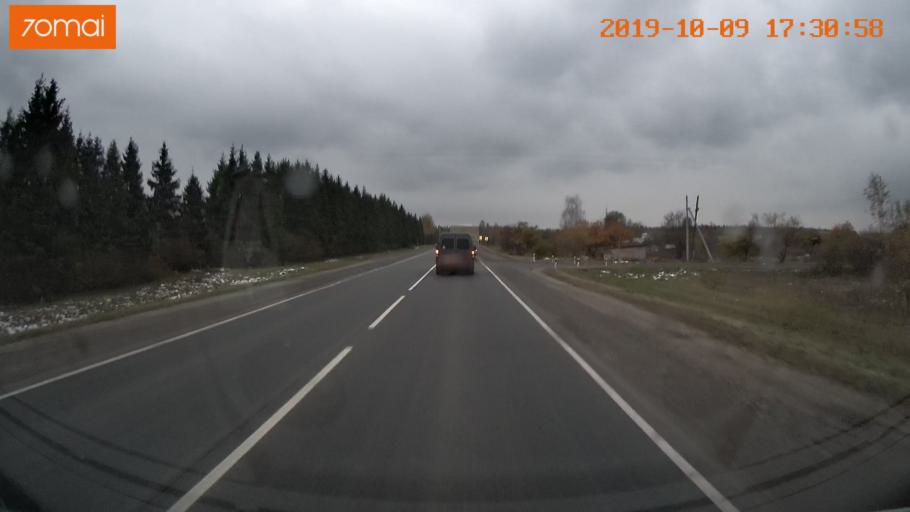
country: RU
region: Ivanovo
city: Bogorodskoye
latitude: 57.1387
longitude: 41.0438
